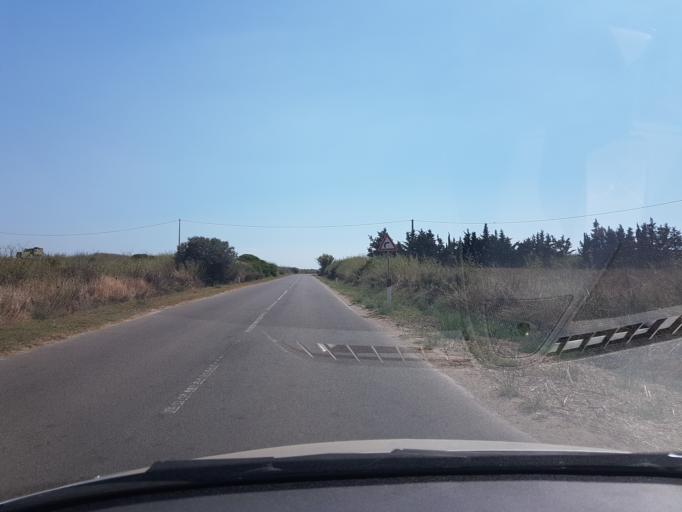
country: IT
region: Sardinia
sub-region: Provincia di Oristano
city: Nurachi
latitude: 39.9801
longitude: 8.4541
